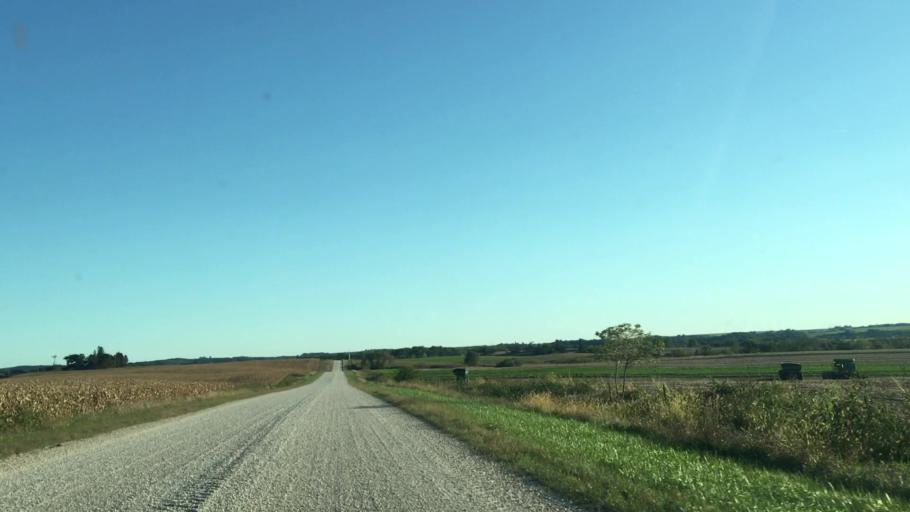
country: US
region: Minnesota
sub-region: Fillmore County
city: Preston
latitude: 43.8022
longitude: -92.0395
